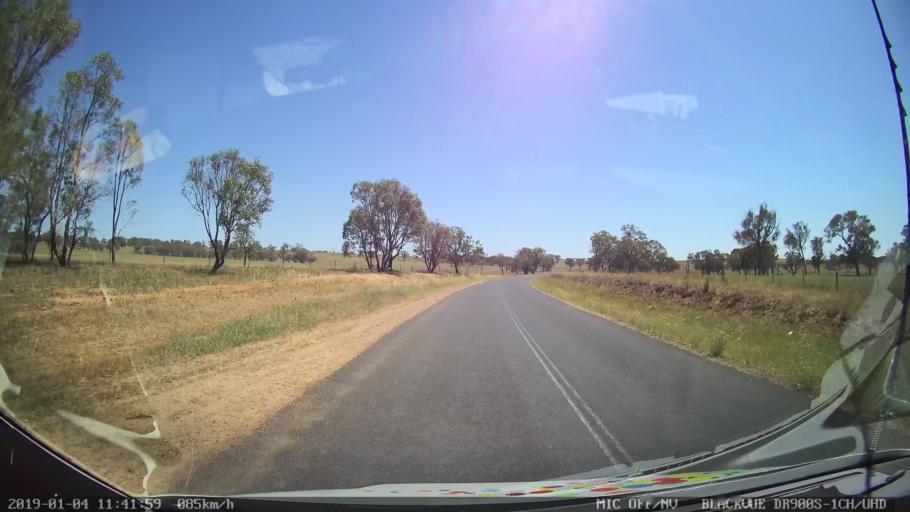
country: AU
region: New South Wales
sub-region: Cabonne
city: Molong
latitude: -32.9873
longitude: 148.7866
